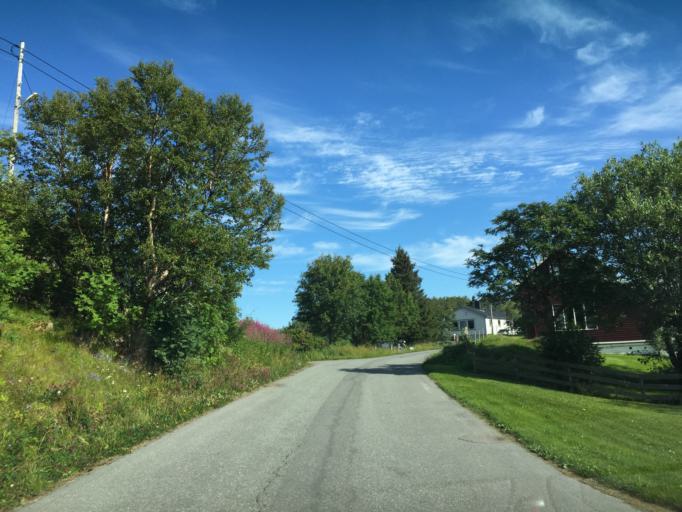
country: NO
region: Nordland
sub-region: Vagan
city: Kabelvag
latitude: 68.3890
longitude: 14.4198
